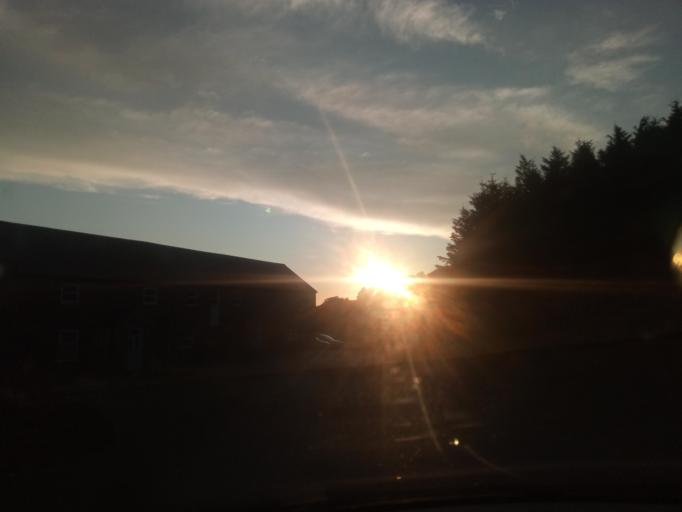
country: GB
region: England
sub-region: Northumberland
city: Bardon Mill
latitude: 54.7985
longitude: -2.3512
